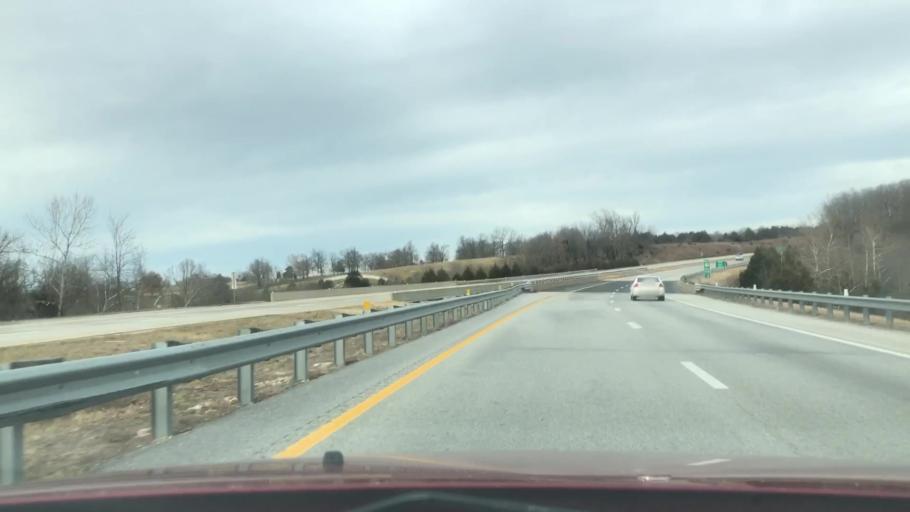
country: US
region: Missouri
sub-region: Greene County
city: Springfield
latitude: 37.2628
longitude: -93.2248
